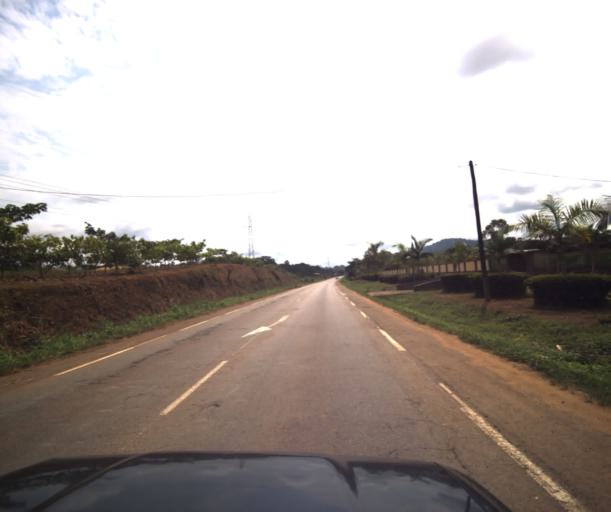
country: CM
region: Centre
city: Eseka
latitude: 3.8554
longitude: 10.5288
